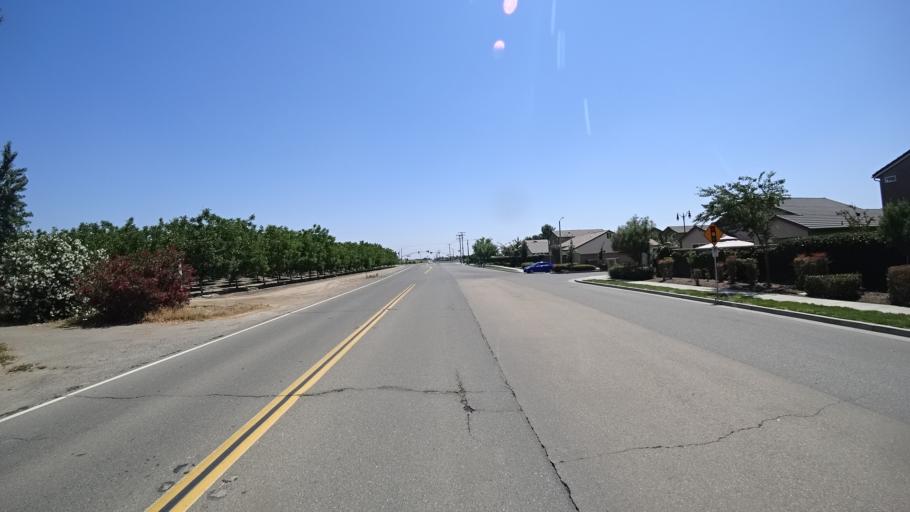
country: US
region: California
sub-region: Kings County
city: Lucerne
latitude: 36.3572
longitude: -119.6754
